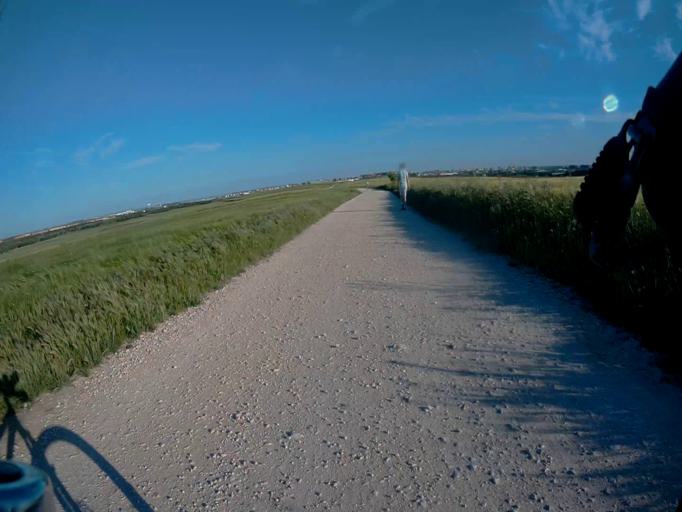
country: ES
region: Madrid
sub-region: Provincia de Madrid
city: Alcorcon
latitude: 40.3261
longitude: -3.8149
